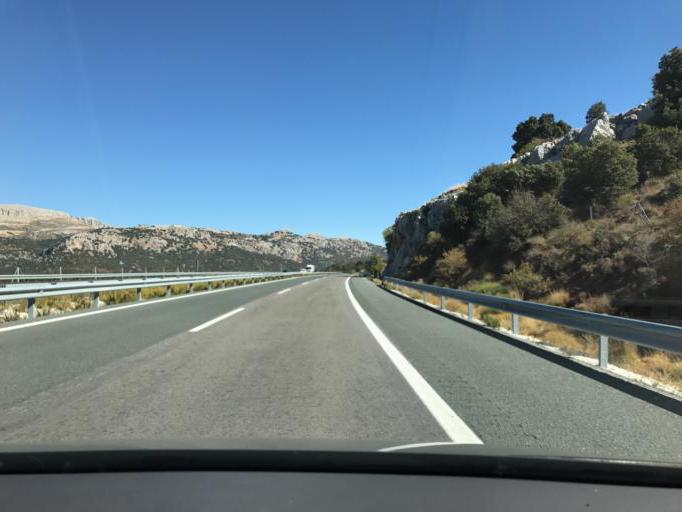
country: ES
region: Andalusia
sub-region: Provincia de Granada
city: Beas de Granada
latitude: 37.2951
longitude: -3.4514
